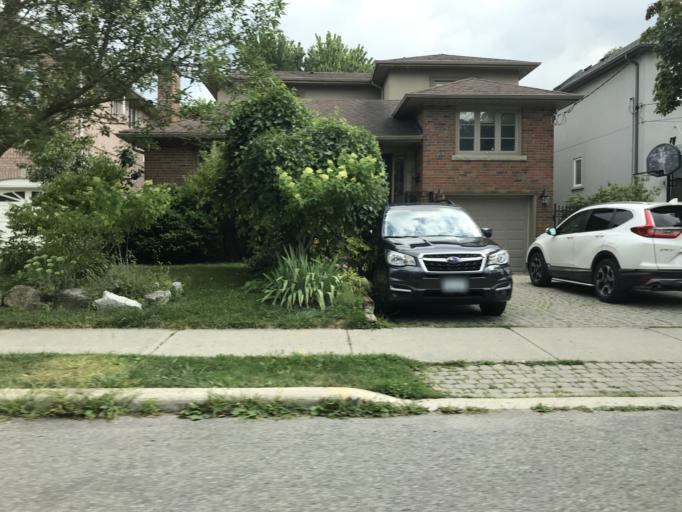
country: CA
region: Ontario
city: North York
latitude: 43.7597
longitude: -79.4154
